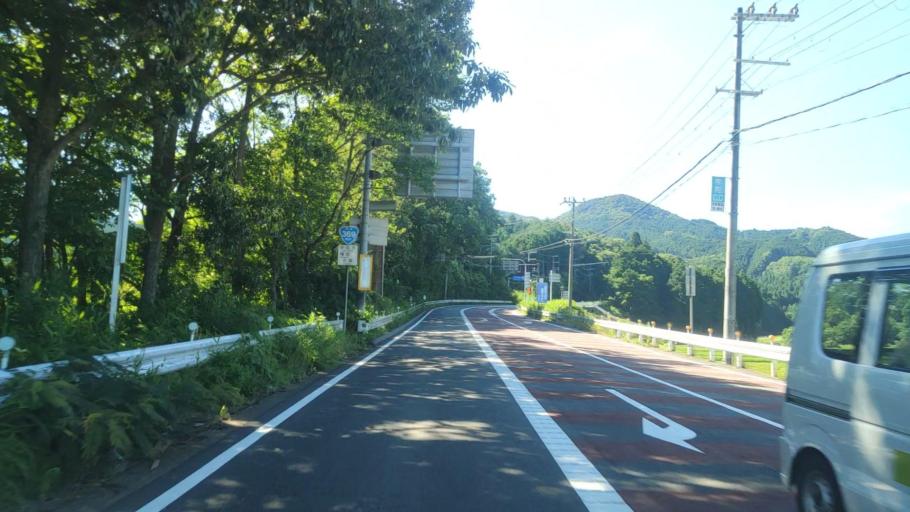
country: JP
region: Nara
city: Haibara-akanedai
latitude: 34.5480
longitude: 135.9612
